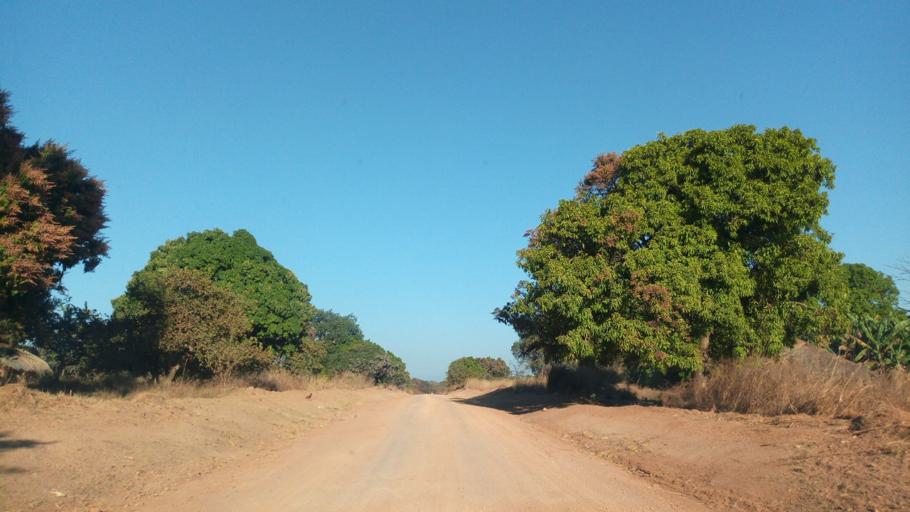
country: ZM
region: Luapula
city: Mwense
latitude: -10.4469
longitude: 28.5643
